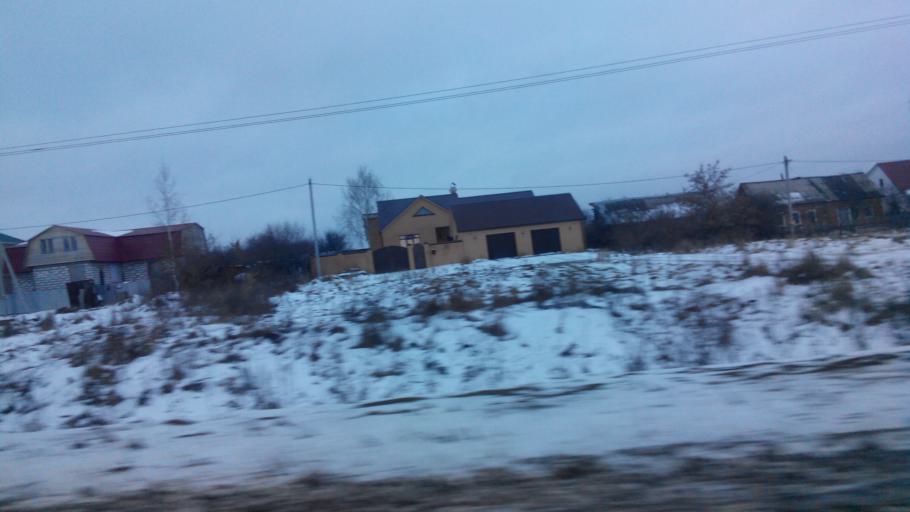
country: RU
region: Tula
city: Mayskiy
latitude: 53.9815
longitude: 38.2211
